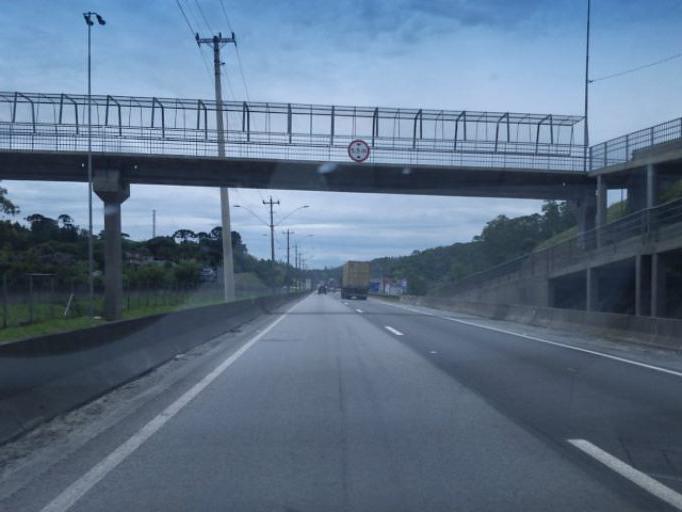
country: BR
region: Sao Paulo
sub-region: Itapecerica Da Serra
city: Itapecerica da Serra
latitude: -23.7604
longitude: -46.9043
